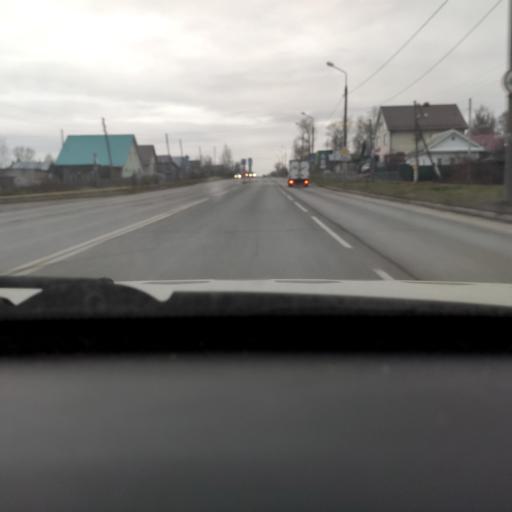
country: RU
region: Perm
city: Polazna
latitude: 58.1137
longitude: 56.4004
